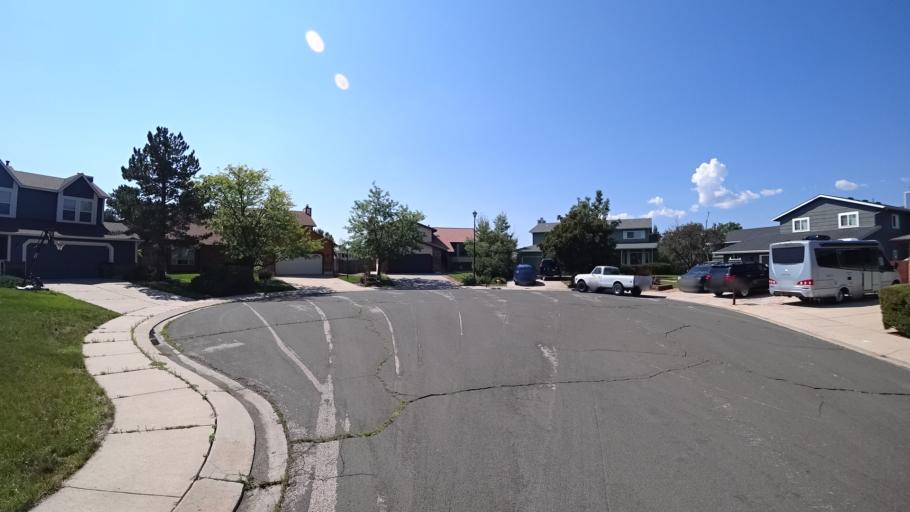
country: US
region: Colorado
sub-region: El Paso County
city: Black Forest
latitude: 38.9576
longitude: -104.7749
